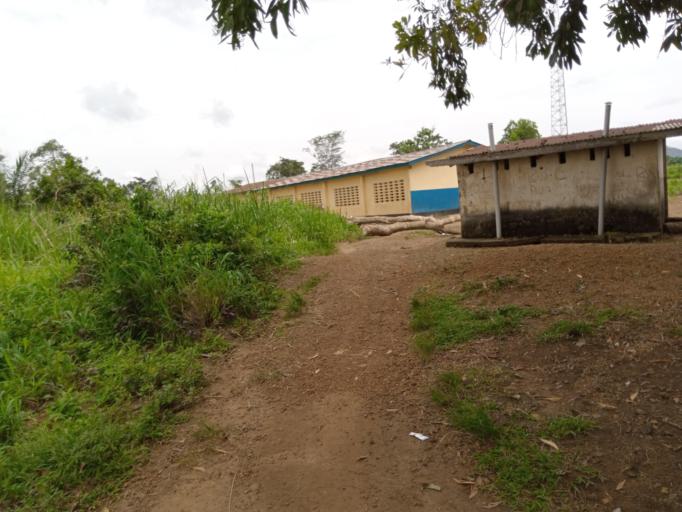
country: SL
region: Southern Province
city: Moyamba
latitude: 8.1653
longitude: -12.4202
